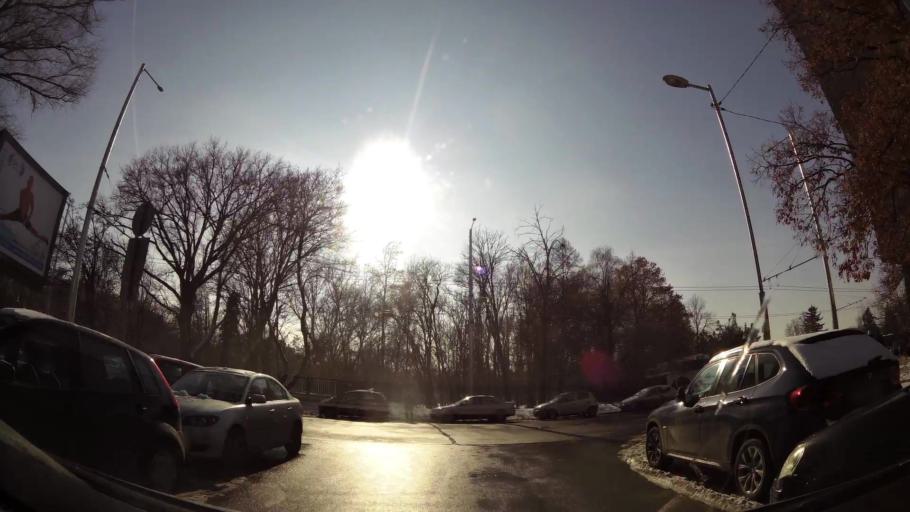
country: BG
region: Sofia-Capital
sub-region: Stolichna Obshtina
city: Sofia
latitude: 42.6746
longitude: 23.3099
